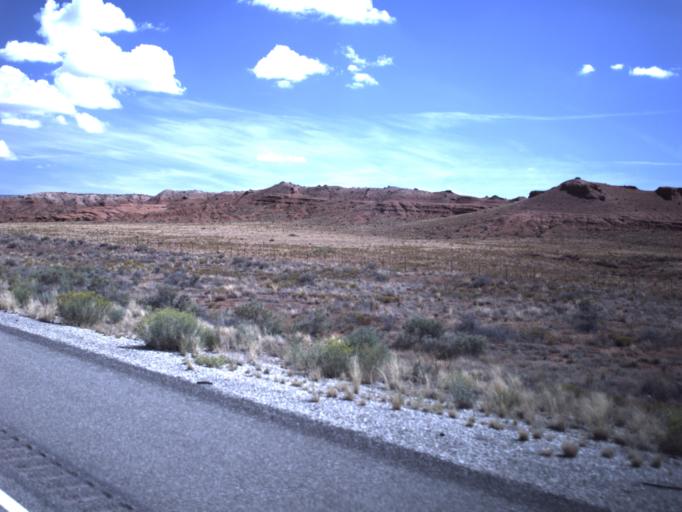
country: US
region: Utah
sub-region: Emery County
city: Ferron
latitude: 38.8454
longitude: -111.0469
